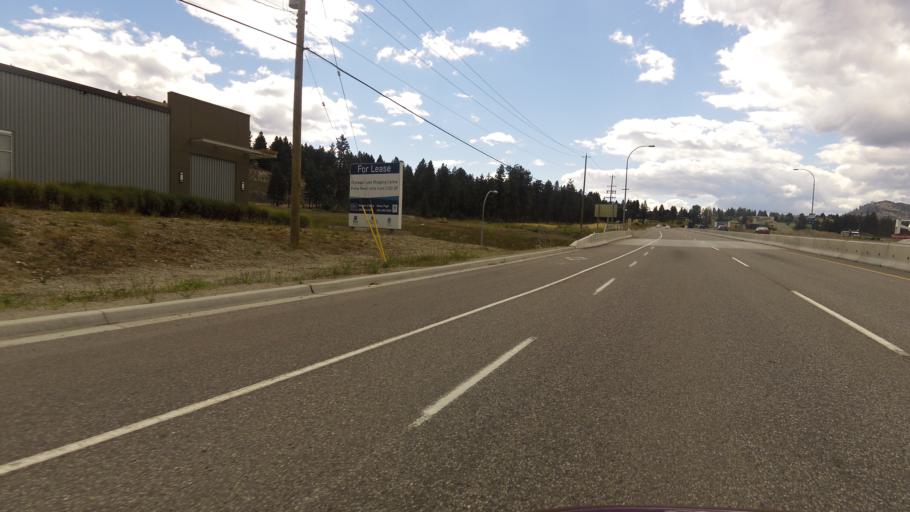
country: CA
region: British Columbia
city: West Kelowna
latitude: 49.8790
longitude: -119.5381
